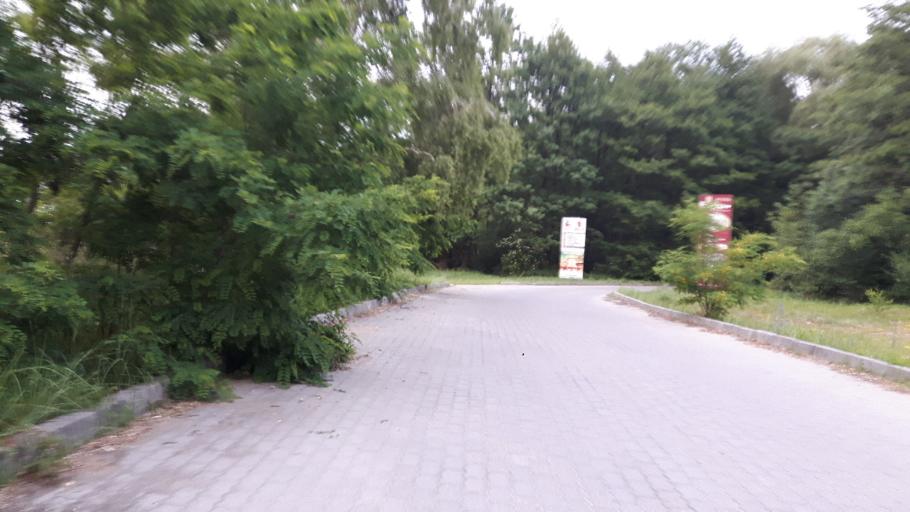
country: RU
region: Kaliningrad
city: Vzmorye
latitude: 54.6511
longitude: 20.3555
